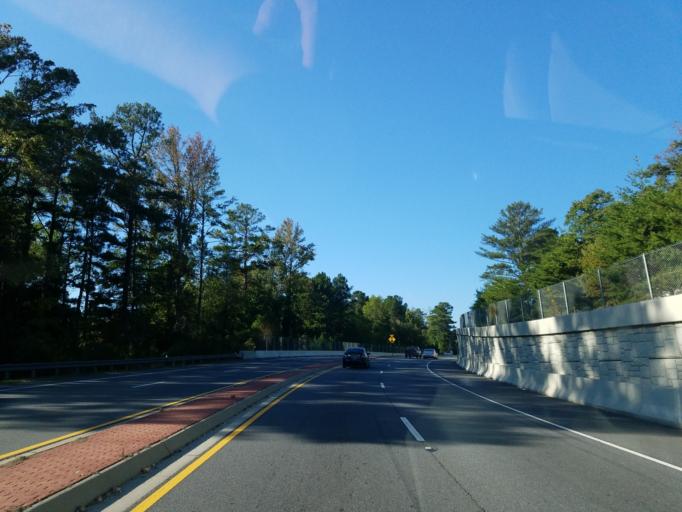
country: US
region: Georgia
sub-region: Cobb County
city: Fair Oaks
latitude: 33.9003
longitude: -84.5990
